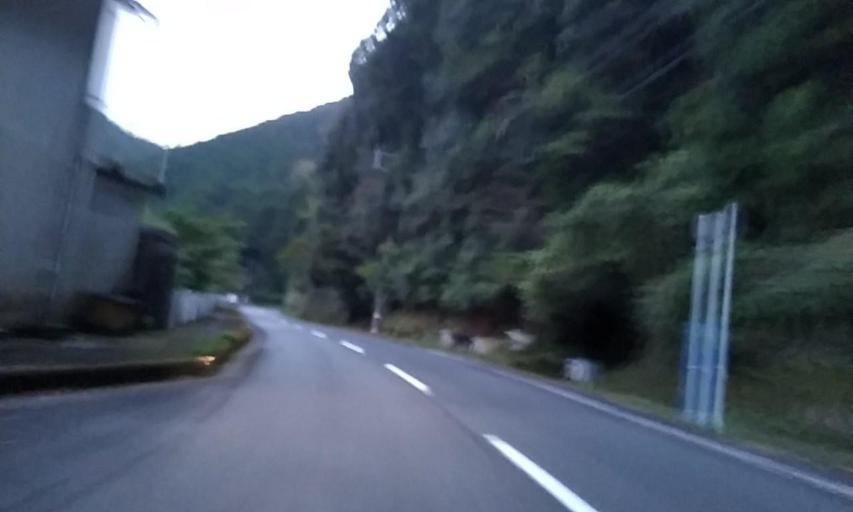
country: JP
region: Wakayama
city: Shingu
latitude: 33.7415
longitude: 135.9335
